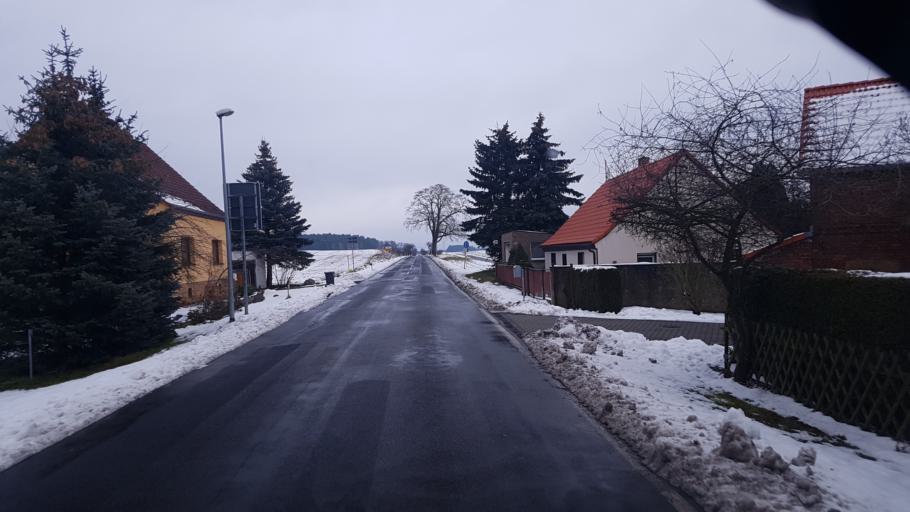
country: DE
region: Brandenburg
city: Lawitz
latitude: 52.0815
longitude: 14.5456
